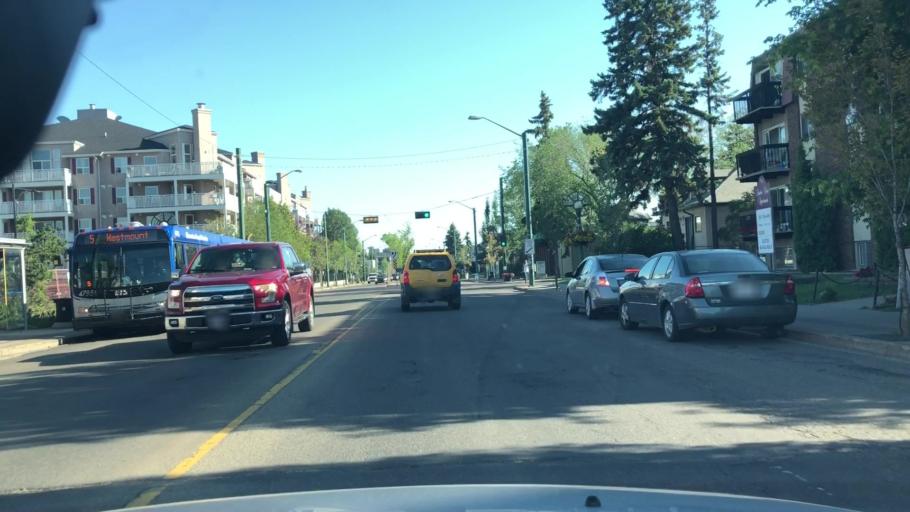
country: CA
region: Alberta
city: Edmonton
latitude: 53.5563
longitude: -113.5359
